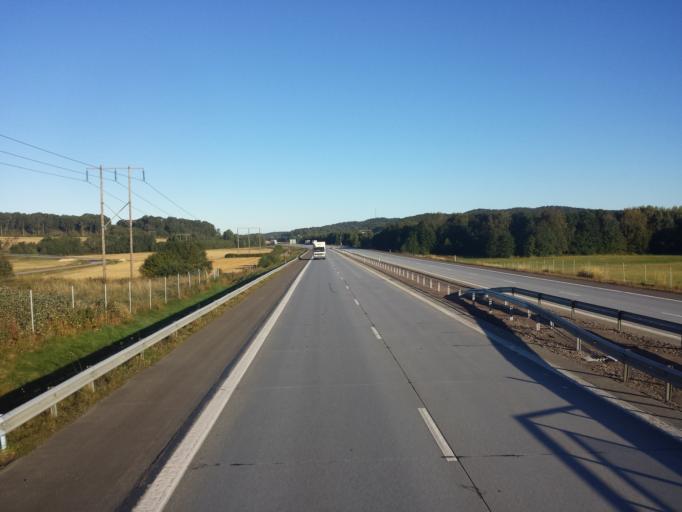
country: SE
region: Halland
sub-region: Halmstads Kommun
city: Getinge
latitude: 56.8589
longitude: 12.6668
